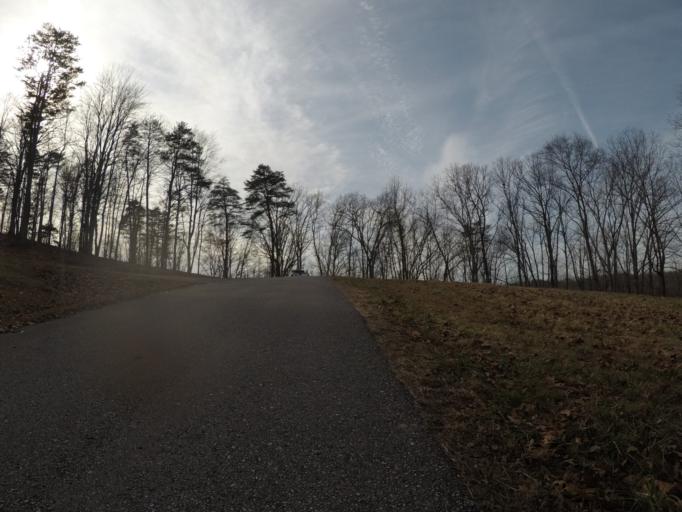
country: US
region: West Virginia
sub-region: Cabell County
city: Huntington
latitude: 38.3842
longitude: -82.3934
